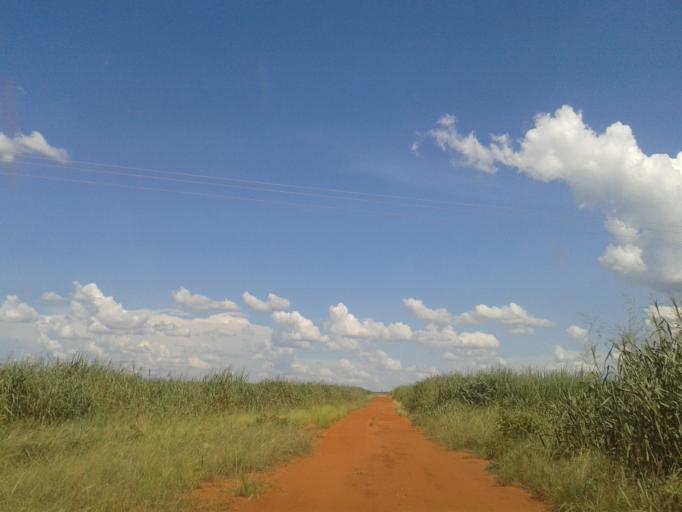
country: BR
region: Minas Gerais
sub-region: Santa Vitoria
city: Santa Vitoria
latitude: -19.1153
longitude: -50.4104
